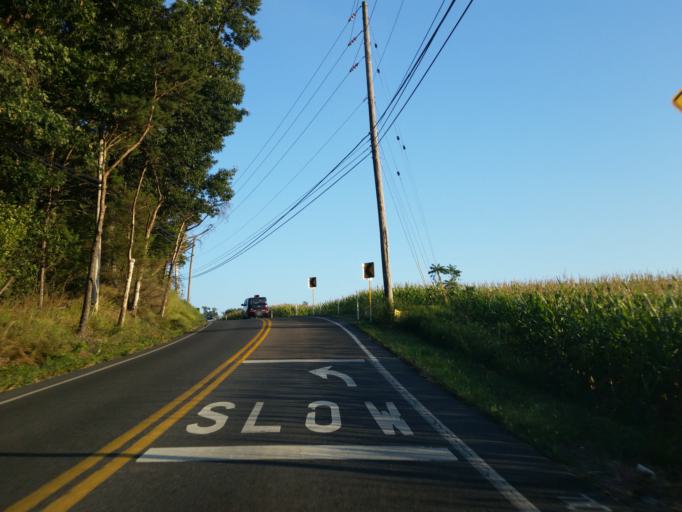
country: US
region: Pennsylvania
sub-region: Lebanon County
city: Jonestown
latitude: 40.3987
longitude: -76.4774
